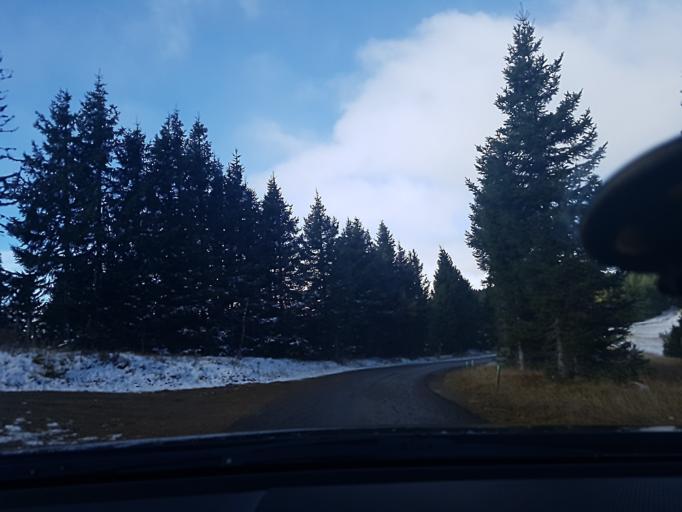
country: AT
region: Styria
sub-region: Politischer Bezirk Murtal
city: Pusterwald
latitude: 47.2706
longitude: 14.4146
